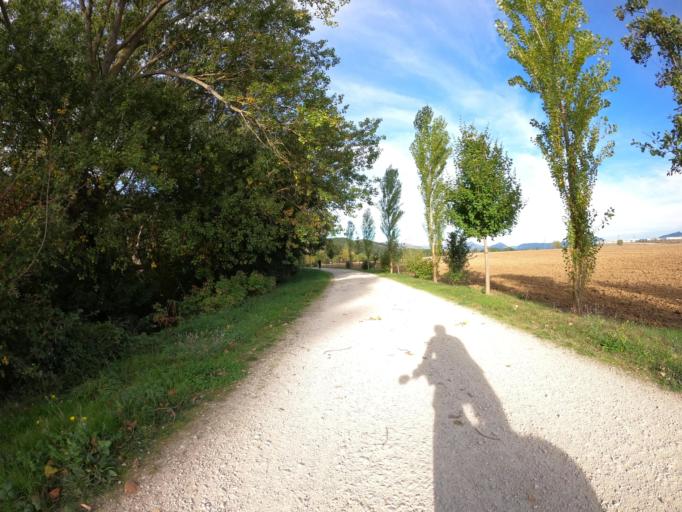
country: ES
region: Navarre
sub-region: Provincia de Navarra
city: Cizur Mayor
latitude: 42.8019
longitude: -1.7057
